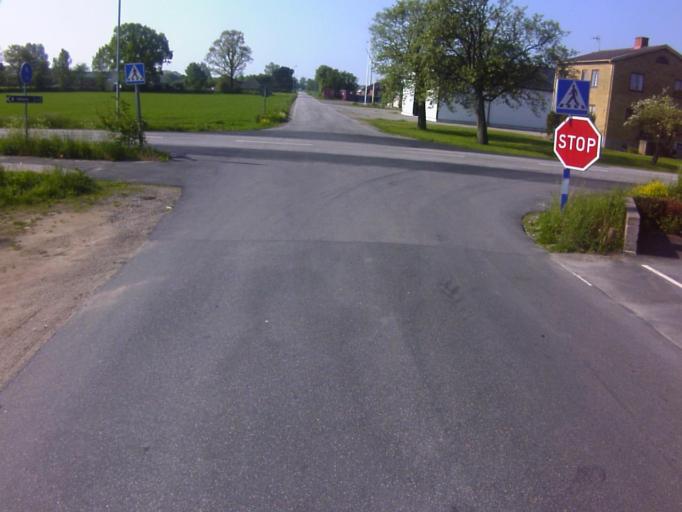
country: SE
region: Blekinge
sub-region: Solvesborgs Kommun
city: Soelvesborg
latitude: 56.0438
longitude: 14.6751
